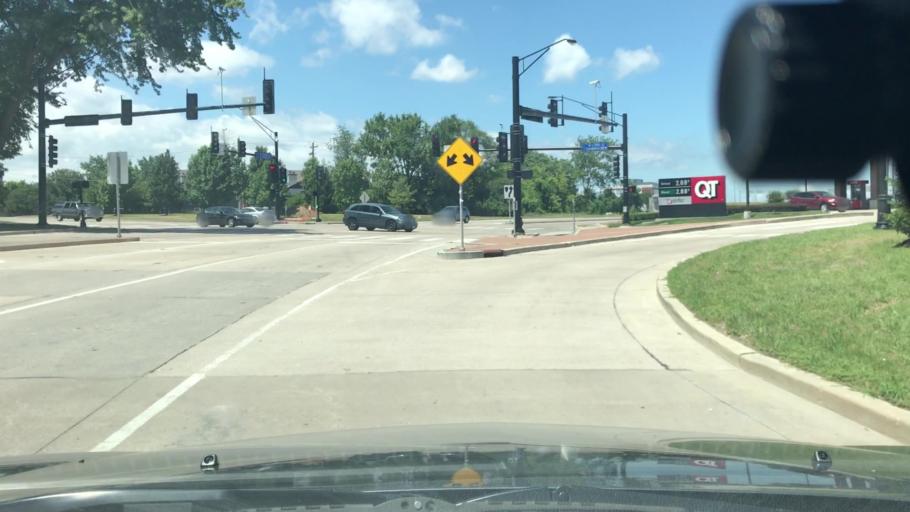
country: US
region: Missouri
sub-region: Saint Charles County
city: Saint Charles
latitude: 38.7646
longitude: -90.4957
